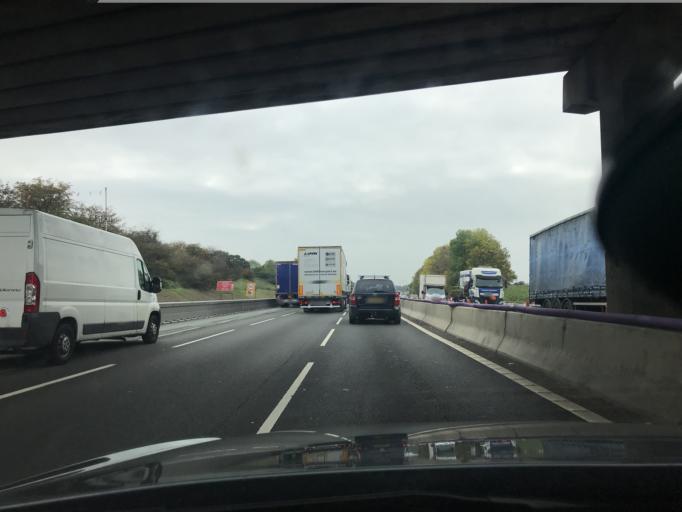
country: GB
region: England
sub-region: Cheshire East
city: Holmes Chapel
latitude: 53.2131
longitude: -2.3885
